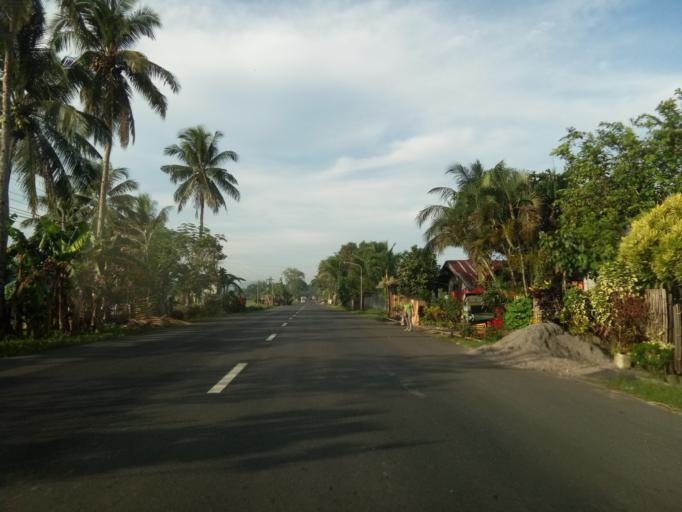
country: PH
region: Caraga
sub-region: Province of Surigao del Norte
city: Tubod
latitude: 9.5459
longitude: 125.5661
